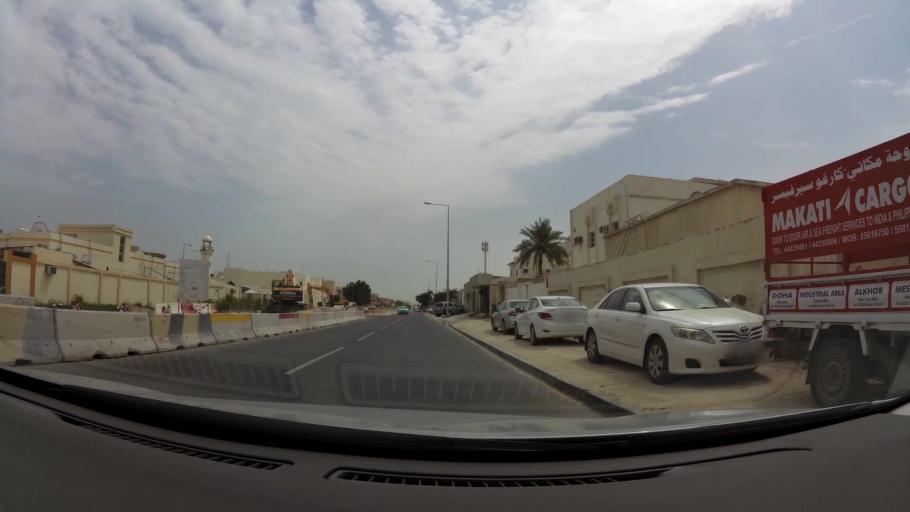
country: QA
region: Baladiyat ar Rayyan
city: Ar Rayyan
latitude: 25.3310
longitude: 51.4732
